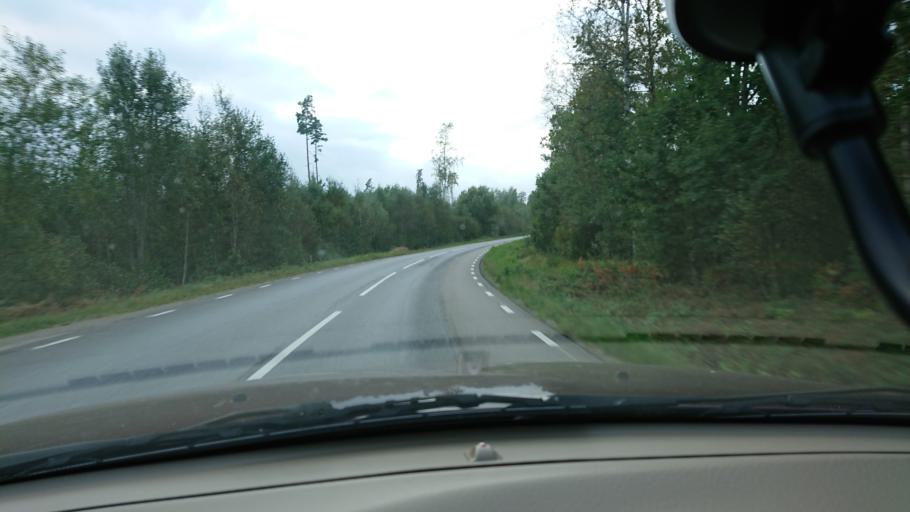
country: SE
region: Kronoberg
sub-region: Vaxjo Kommun
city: Lammhult
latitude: 57.0838
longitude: 14.7037
